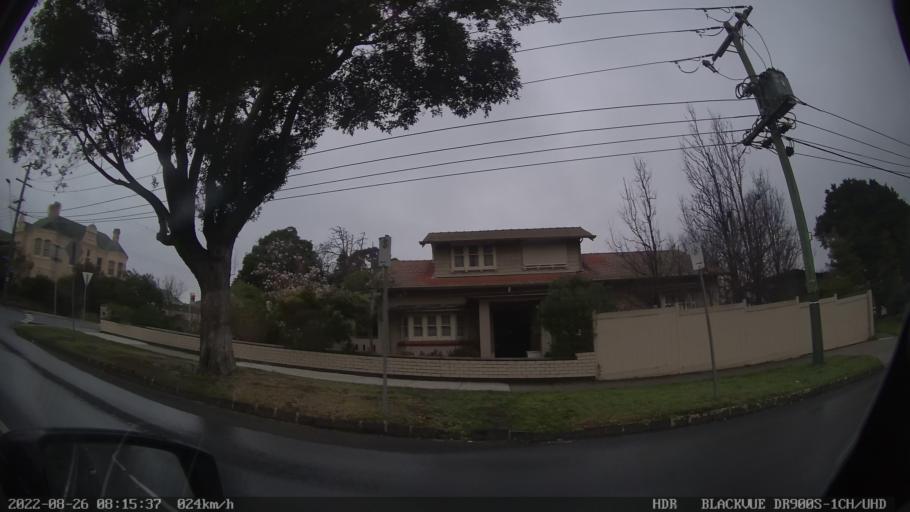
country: AU
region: Victoria
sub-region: Glen Eira
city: Elsternwick
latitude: -37.8922
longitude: 145.0086
